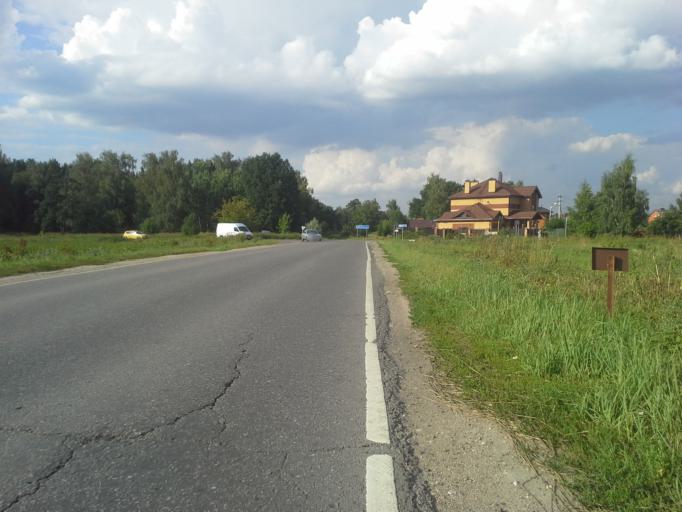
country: RU
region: Moskovskaya
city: Dubrovitsy
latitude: 55.4466
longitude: 37.4787
